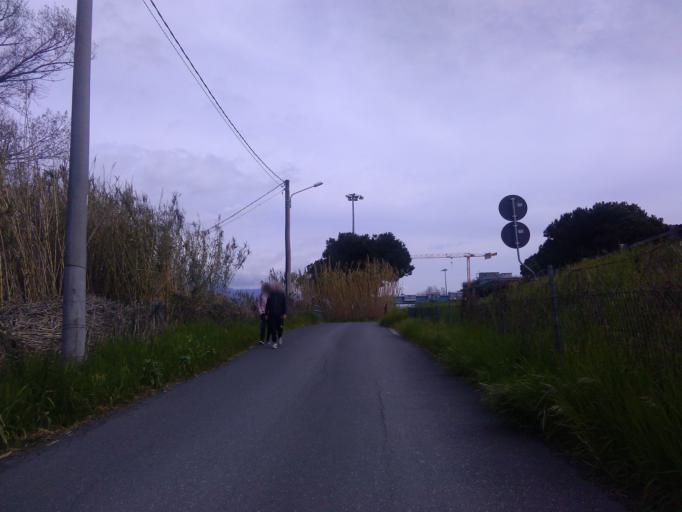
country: IT
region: Tuscany
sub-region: Provincia di Massa-Carrara
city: Marina di Carrara
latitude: 44.0542
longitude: 10.0343
